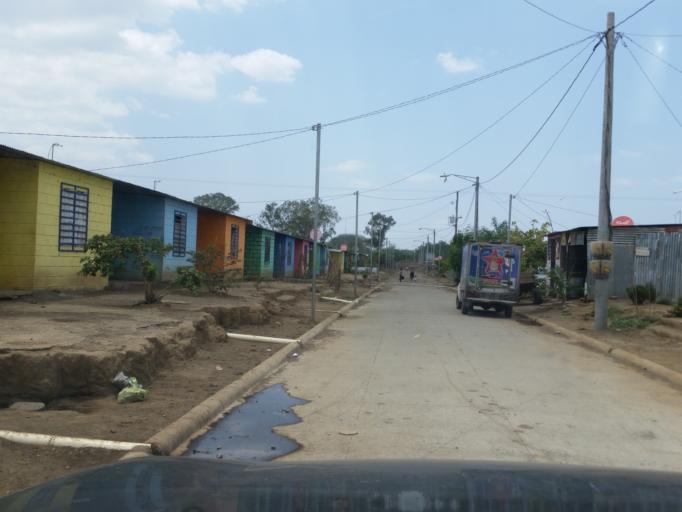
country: NI
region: Managua
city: Tipitapa
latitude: 12.1282
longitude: -86.1572
